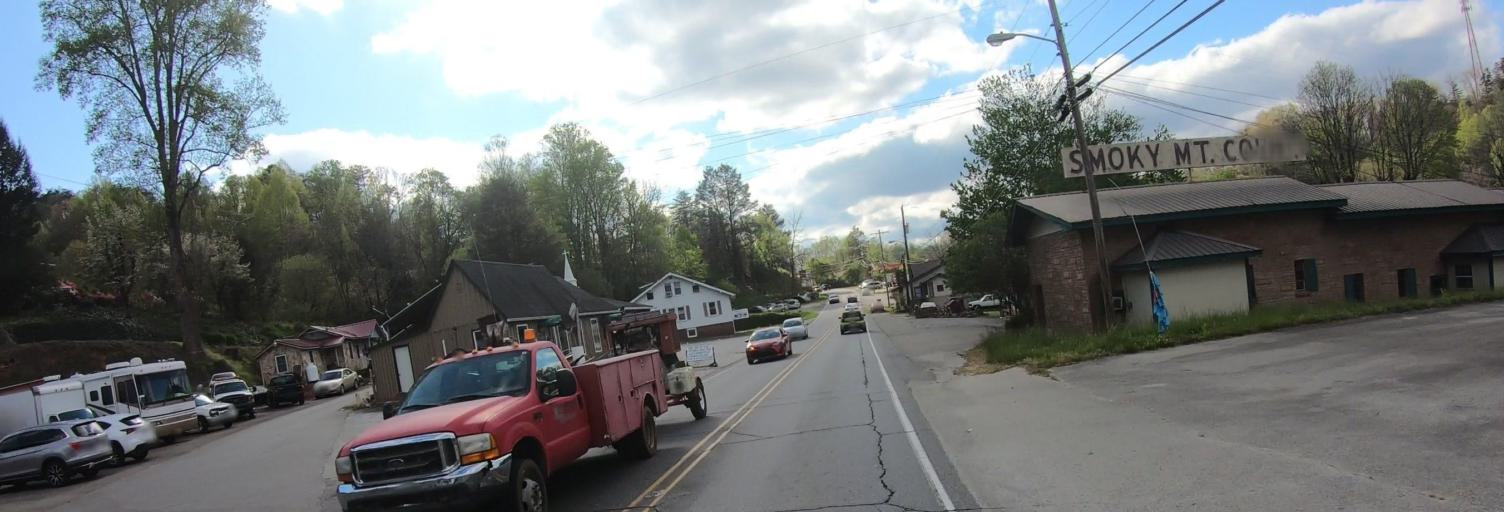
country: US
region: North Carolina
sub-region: Swain County
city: Bryson City
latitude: 35.4322
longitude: -83.4331
